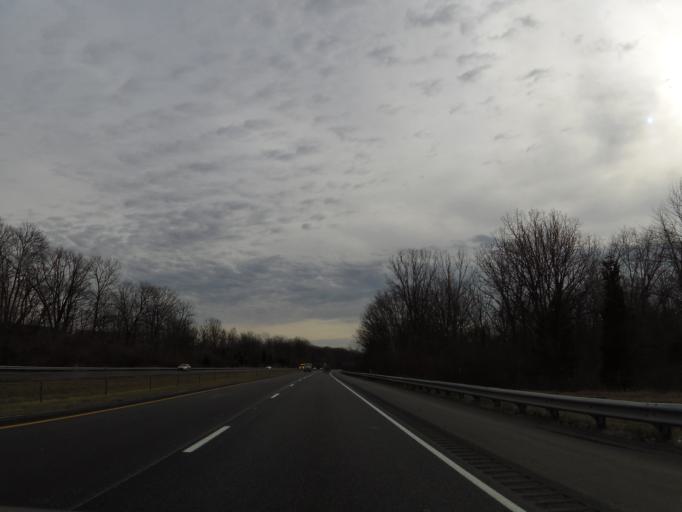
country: US
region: Indiana
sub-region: Marion County
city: Clermont
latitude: 39.8285
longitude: -86.3191
